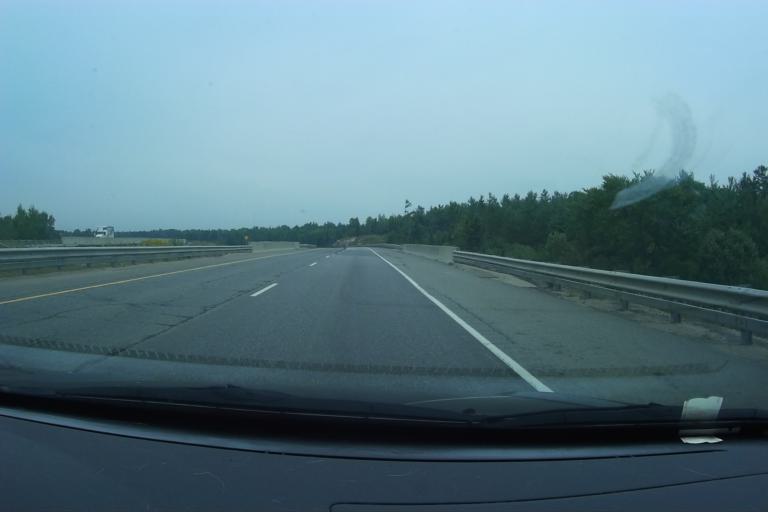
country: CA
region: Ontario
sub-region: Nipissing District
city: North Bay
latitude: 46.2738
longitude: -79.4011
